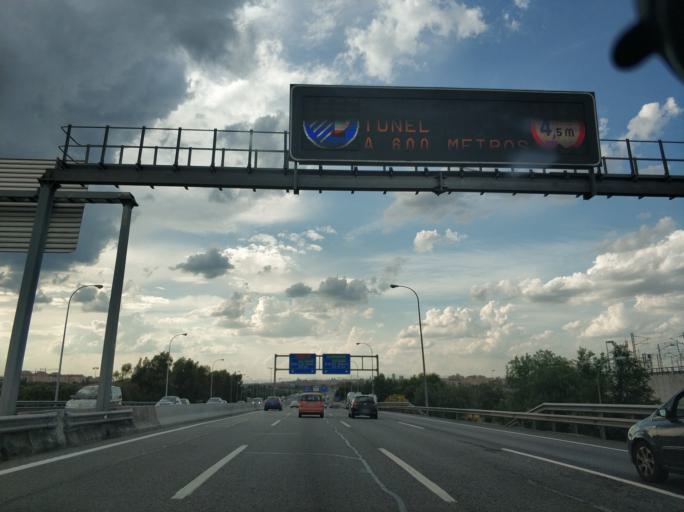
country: ES
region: Madrid
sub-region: Provincia de Madrid
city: Usera
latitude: 40.3746
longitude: -3.6820
